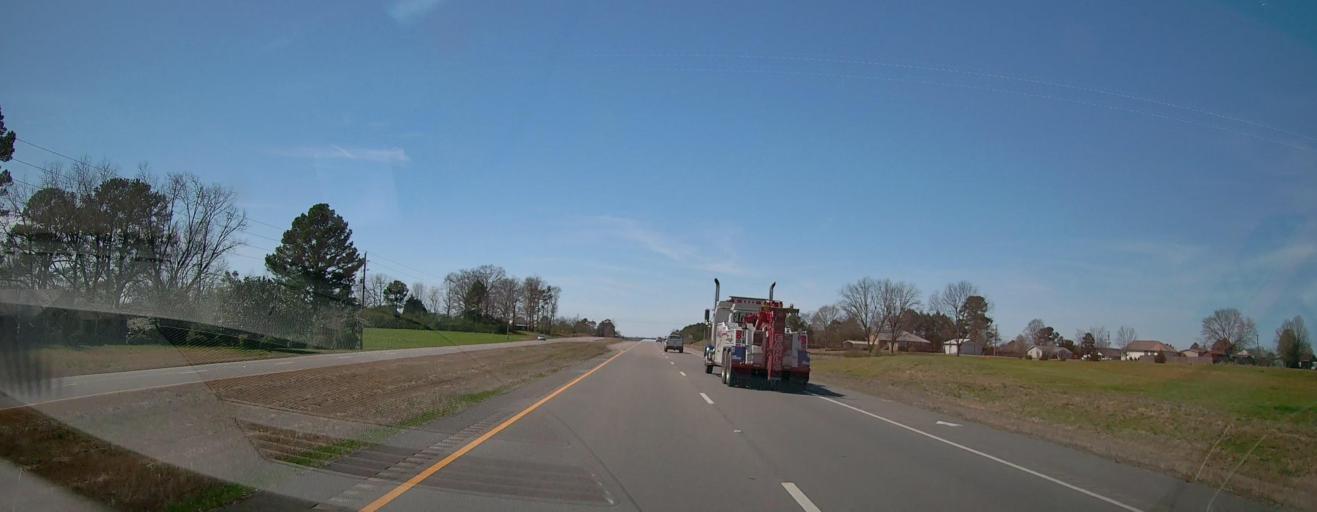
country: US
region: Alabama
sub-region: Cullman County
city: Cullman
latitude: 34.1801
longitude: -86.7528
